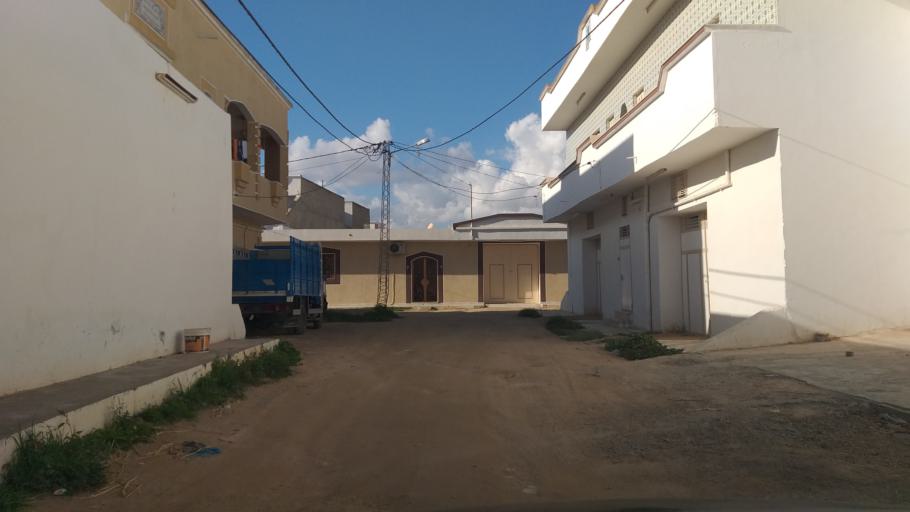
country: TN
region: Al Mahdiyah
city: El Jem
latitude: 35.2903
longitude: 10.7123
